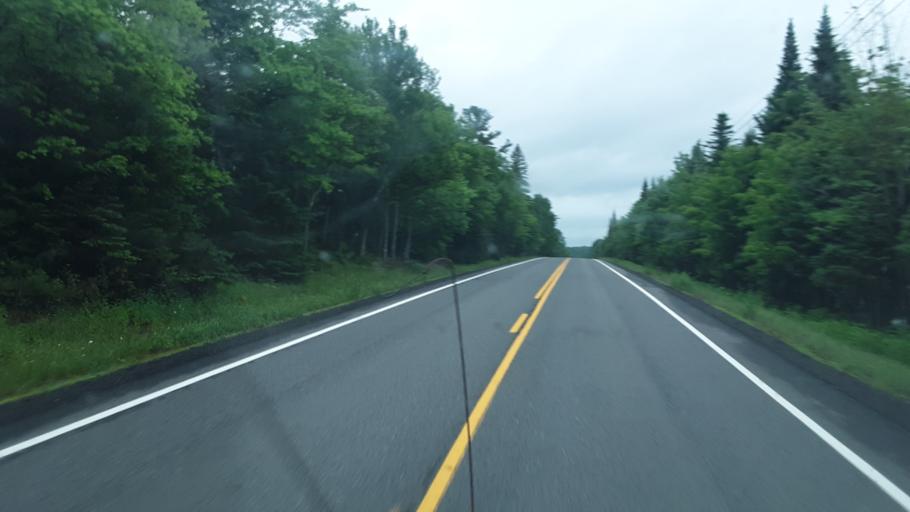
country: US
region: Maine
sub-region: Penobscot County
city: Patten
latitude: 46.3021
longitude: -68.3572
